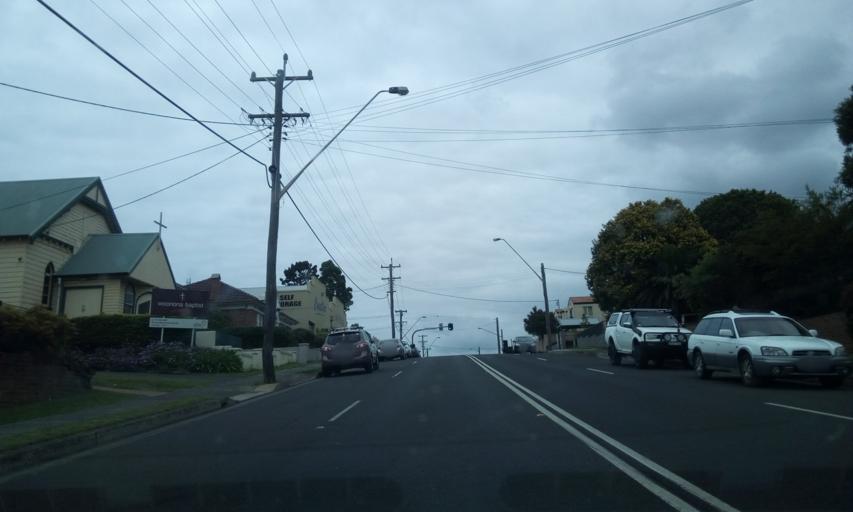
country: AU
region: New South Wales
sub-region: Wollongong
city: Bulli
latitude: -34.3459
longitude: 150.9042
